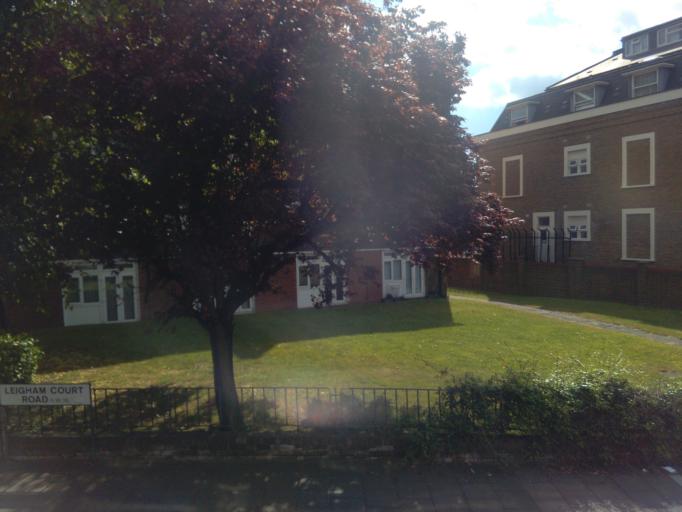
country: GB
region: England
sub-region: Greater London
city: Brixton Hill
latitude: 51.4354
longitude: -0.1241
